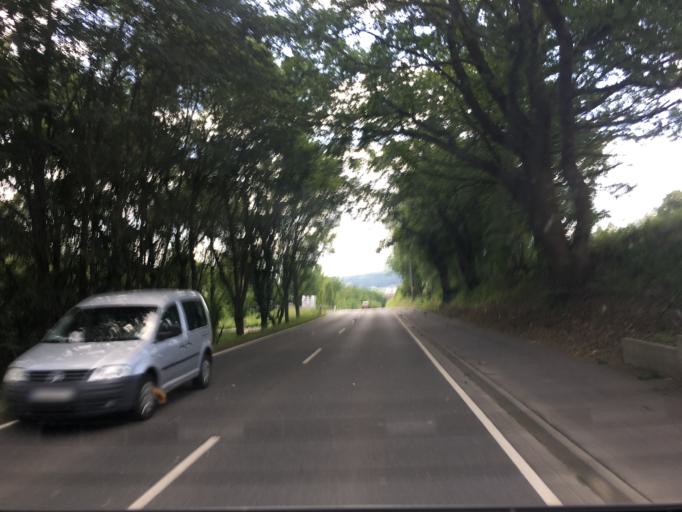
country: DE
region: Rheinland-Pfalz
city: Bad Neuenahr-Ahrweiler
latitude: 50.5549
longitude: 7.1135
